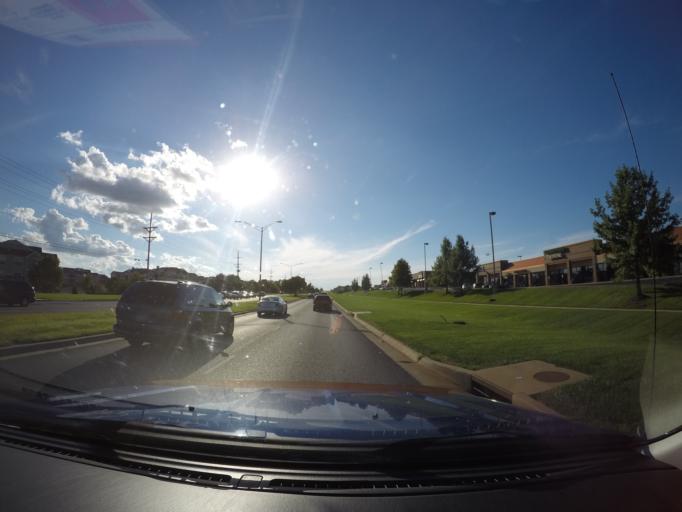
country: US
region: Kansas
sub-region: Johnson County
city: Lenexa
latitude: 38.8838
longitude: -94.7243
